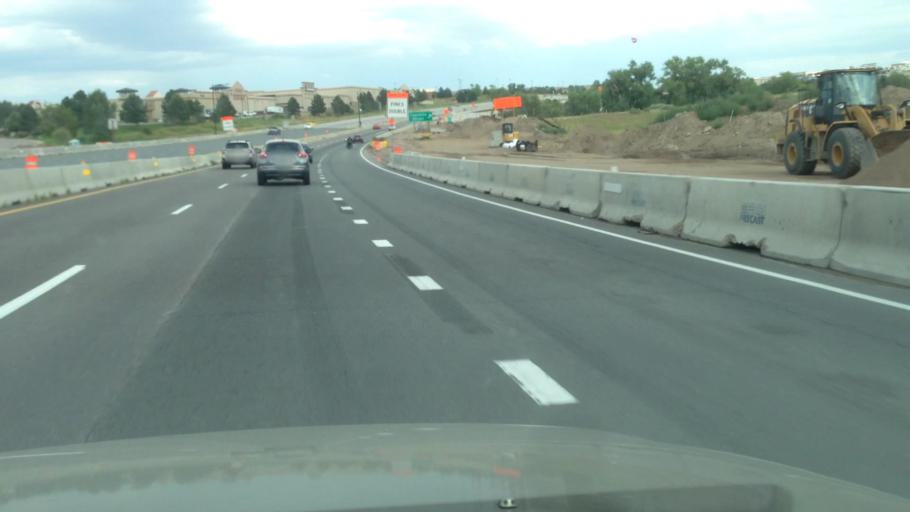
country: US
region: Colorado
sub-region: Douglas County
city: Acres Green
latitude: 39.5640
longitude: -104.8905
